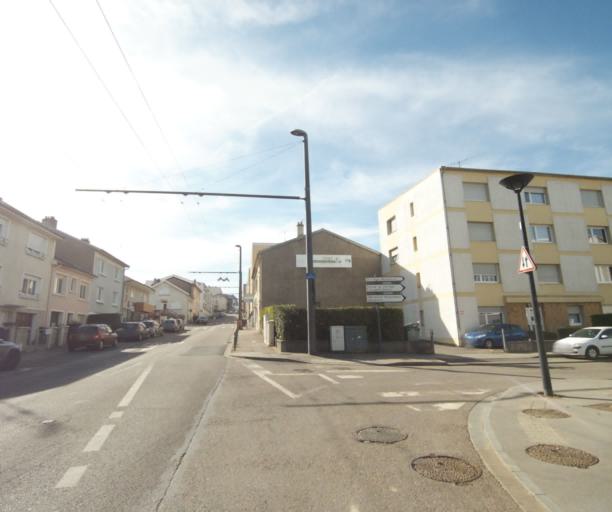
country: FR
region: Lorraine
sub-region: Departement de Meurthe-et-Moselle
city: Villers-les-Nancy
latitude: 48.6657
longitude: 6.1654
